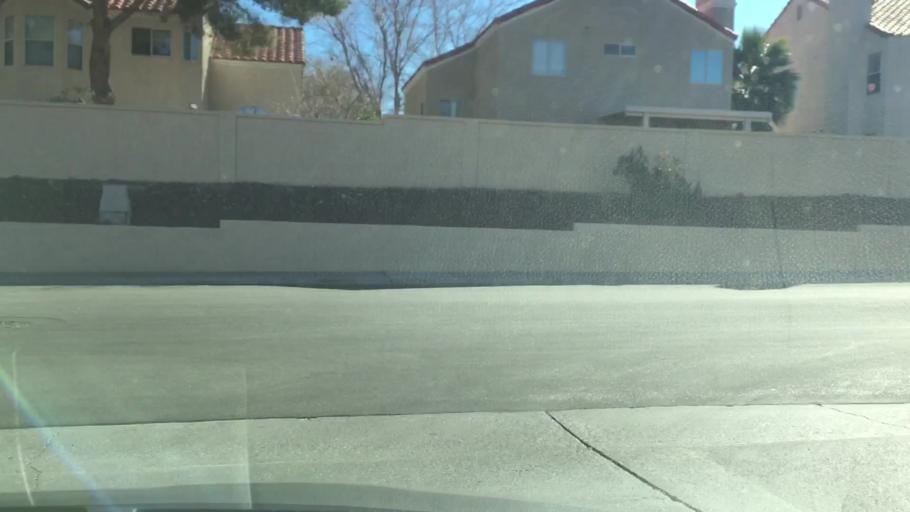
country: US
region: Nevada
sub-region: Clark County
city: Whitney
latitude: 36.0613
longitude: -115.0604
